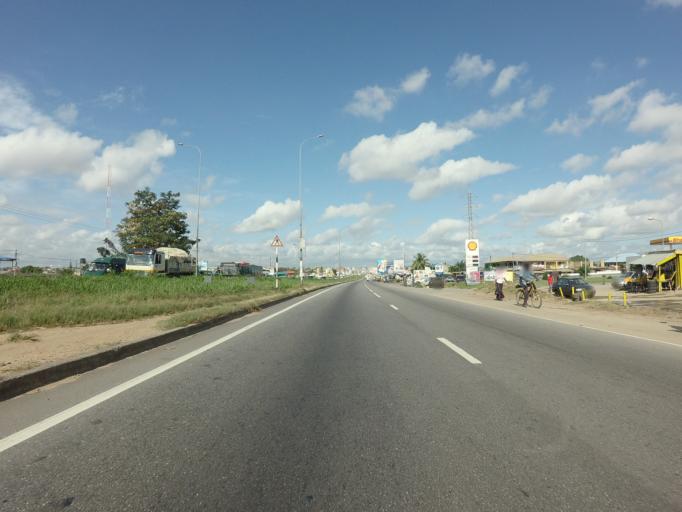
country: GH
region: Central
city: Kasoa
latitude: 5.5357
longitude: -0.4115
